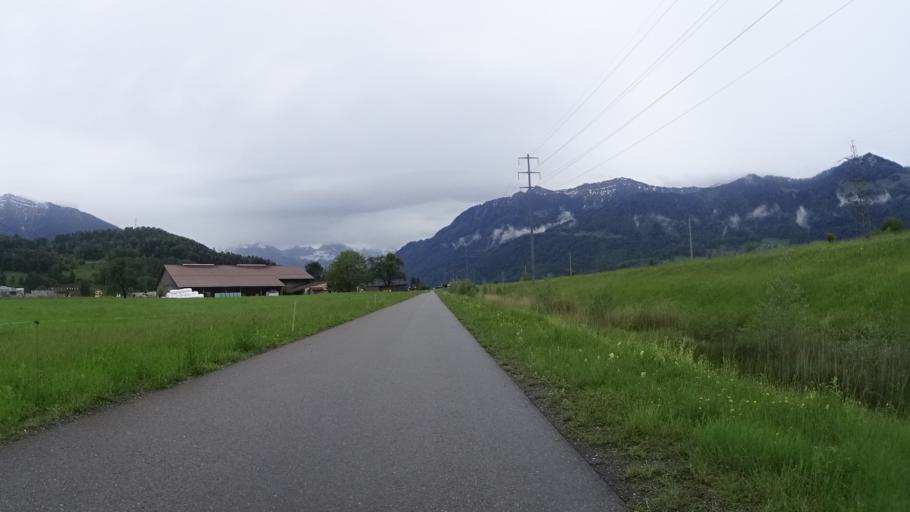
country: CH
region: Saint Gallen
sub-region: Wahlkreis See-Gaster
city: Benken
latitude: 47.1922
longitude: 8.9890
